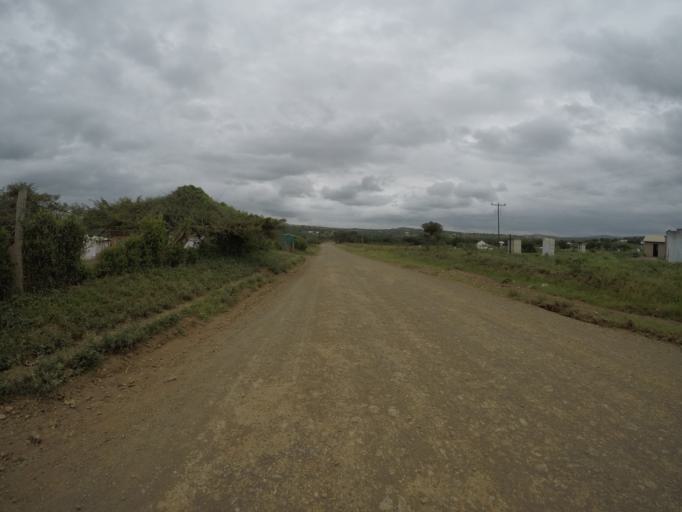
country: ZA
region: KwaZulu-Natal
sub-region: uThungulu District Municipality
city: Empangeni
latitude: -28.5849
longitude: 31.8454
